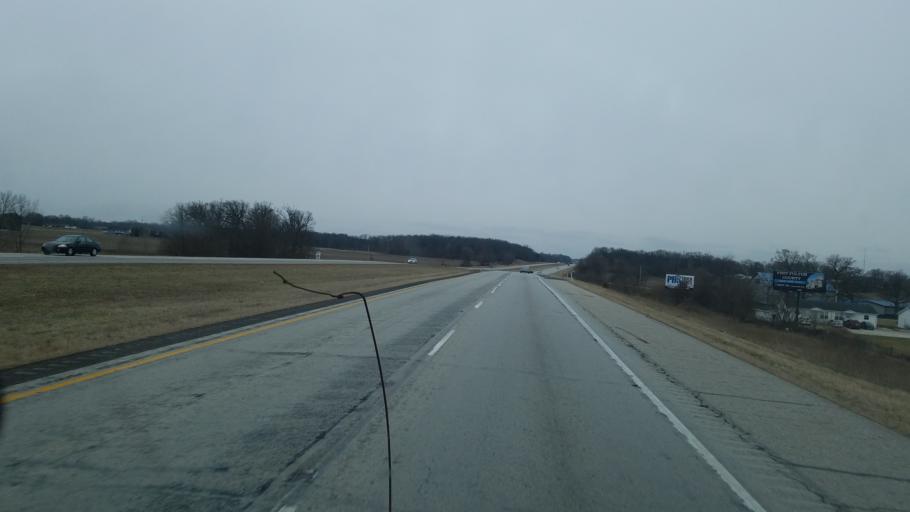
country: US
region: Indiana
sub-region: Fulton County
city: Rochester
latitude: 41.0787
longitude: -86.2405
